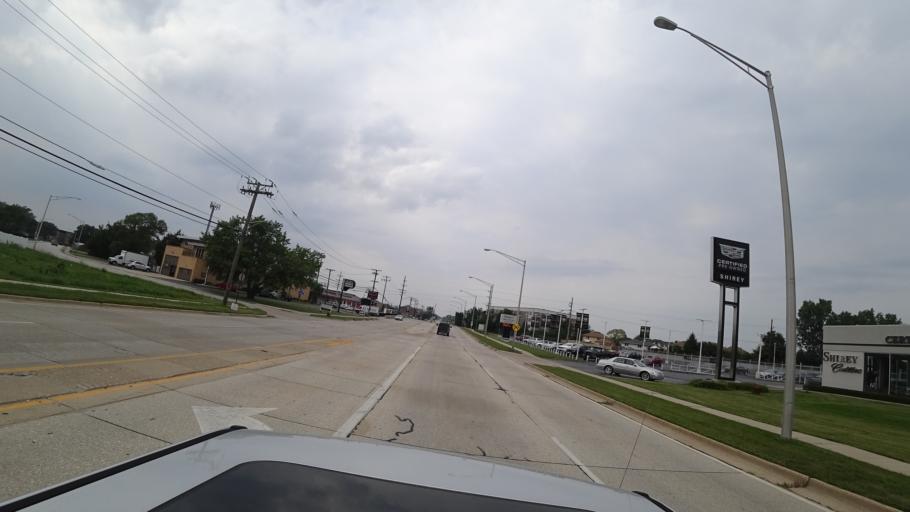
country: US
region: Illinois
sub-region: Cook County
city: Oak Lawn
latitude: 41.6944
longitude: -87.7593
